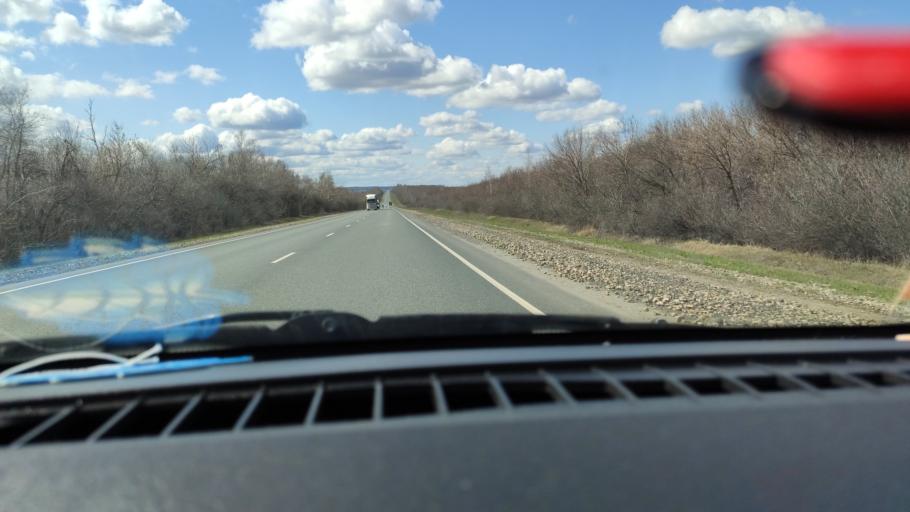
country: RU
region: Saratov
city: Khvalynsk
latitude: 52.6087
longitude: 48.1557
